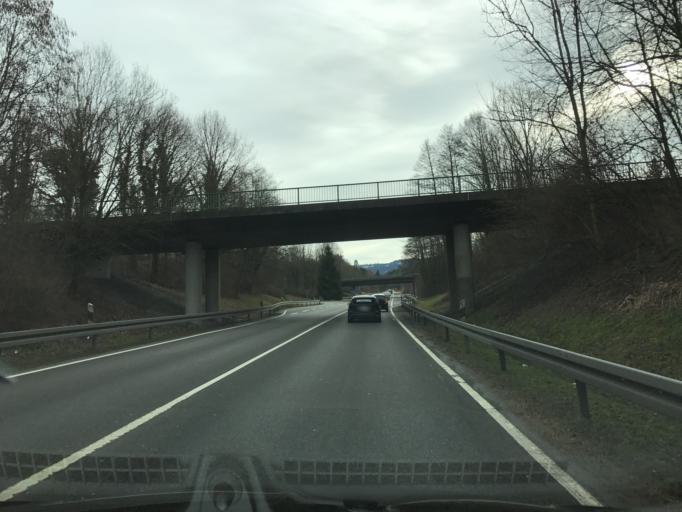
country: DE
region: Bavaria
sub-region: Swabia
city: Weissensberg
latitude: 47.5763
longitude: 9.7079
